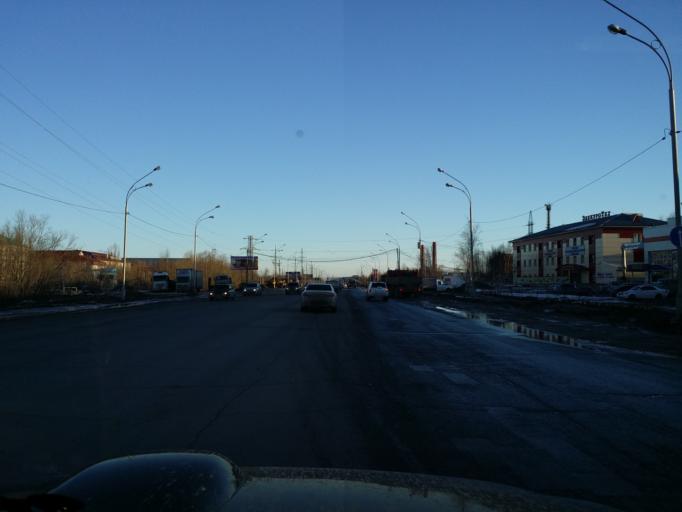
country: RU
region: Khanty-Mansiyskiy Avtonomnyy Okrug
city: Nizhnevartovsk
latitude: 60.9551
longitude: 76.5300
